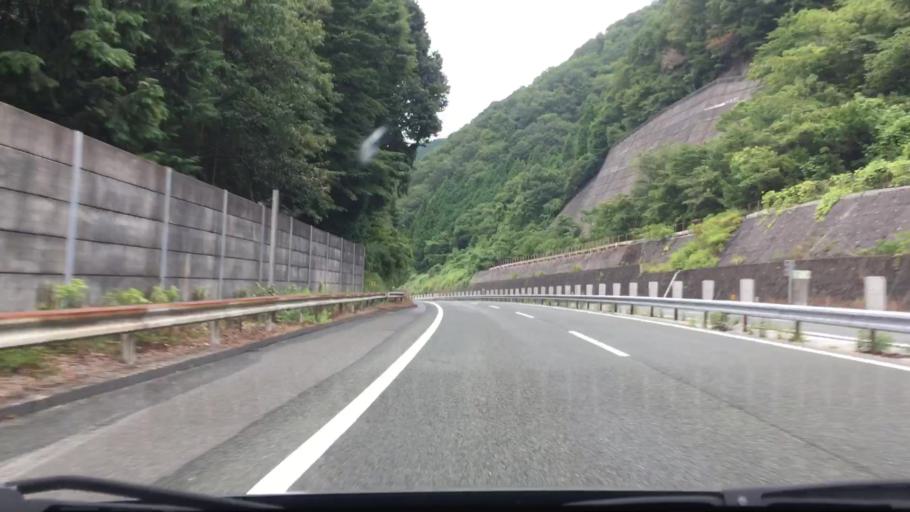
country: JP
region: Okayama
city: Niimi
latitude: 34.9812
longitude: 133.3762
